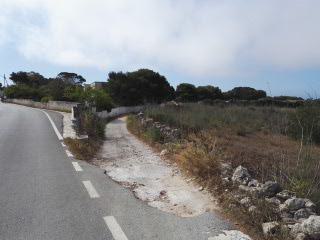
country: IT
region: Sicily
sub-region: Trapani
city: Favignana
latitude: 37.9217
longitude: 12.3424
